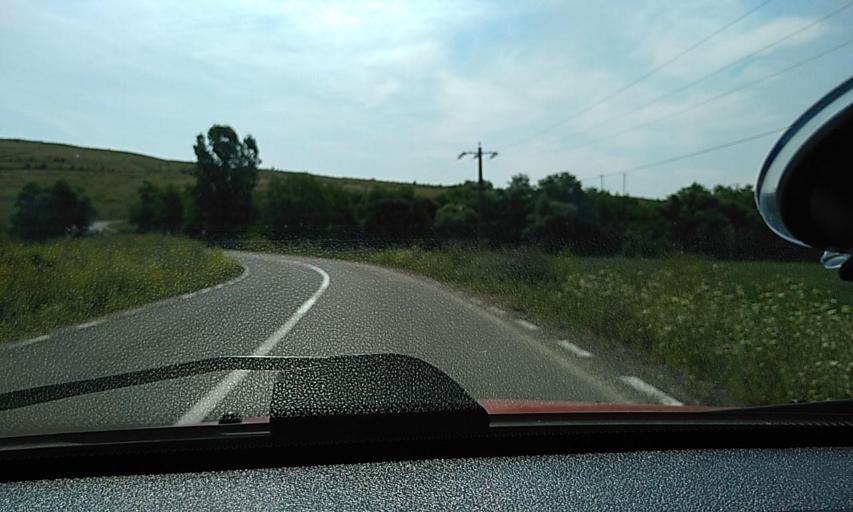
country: RO
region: Brasov
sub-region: Oras Rupea
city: Fiser
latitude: 46.0371
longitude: 25.1347
